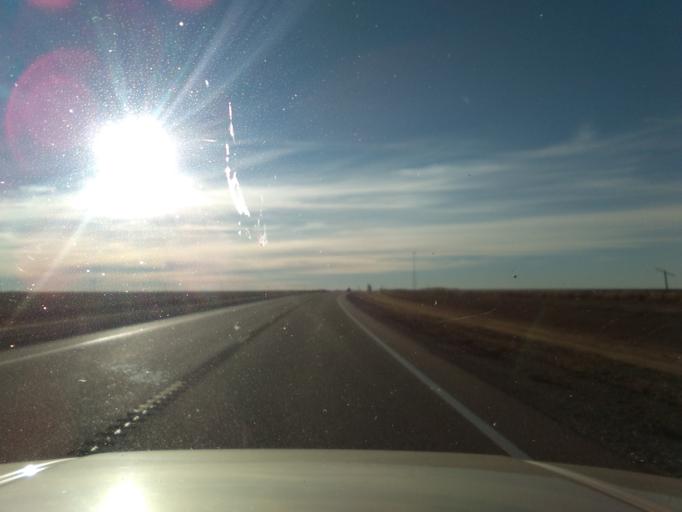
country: US
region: Kansas
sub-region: Sheridan County
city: Hoxie
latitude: 39.4852
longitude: -100.7036
